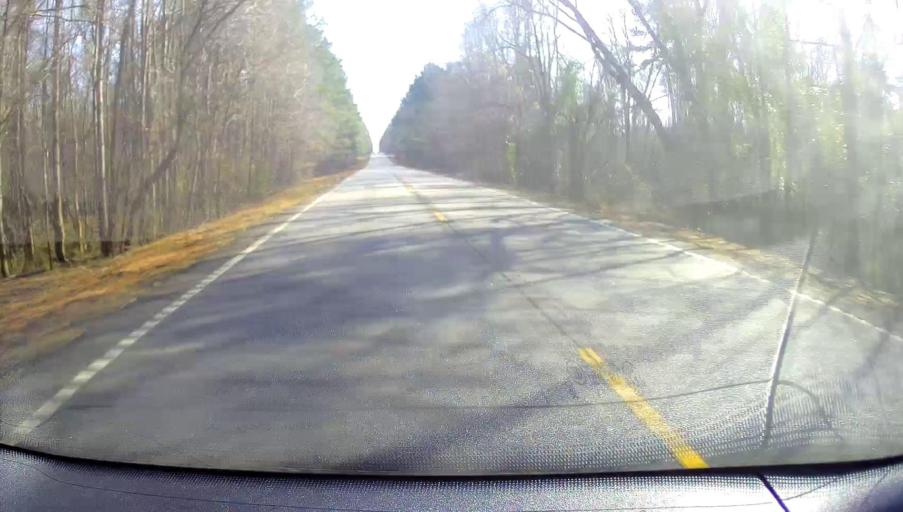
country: US
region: Georgia
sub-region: Butts County
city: Indian Springs
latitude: 33.1655
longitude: -83.8419
